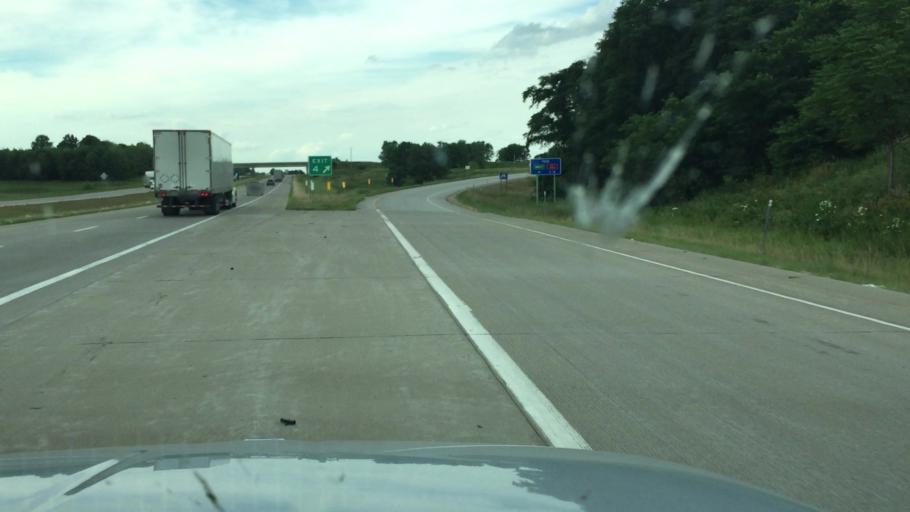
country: US
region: Iowa
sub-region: Scott County
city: Buffalo
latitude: 41.5339
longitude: -90.6754
